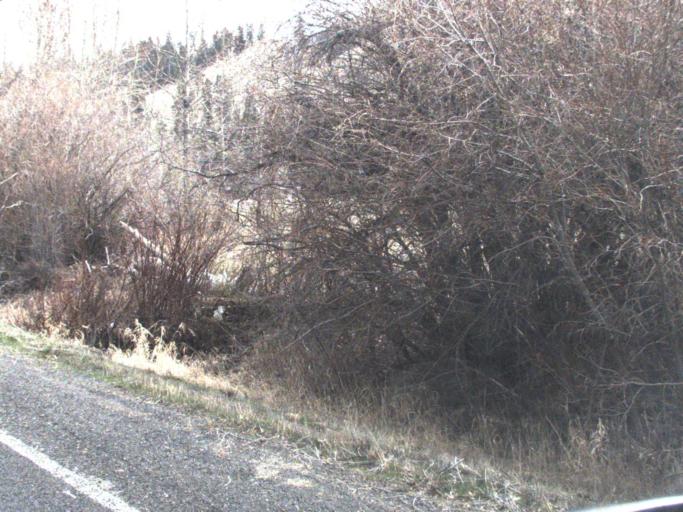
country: US
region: Washington
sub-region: Yakima County
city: Tieton
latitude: 46.7980
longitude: -120.8947
